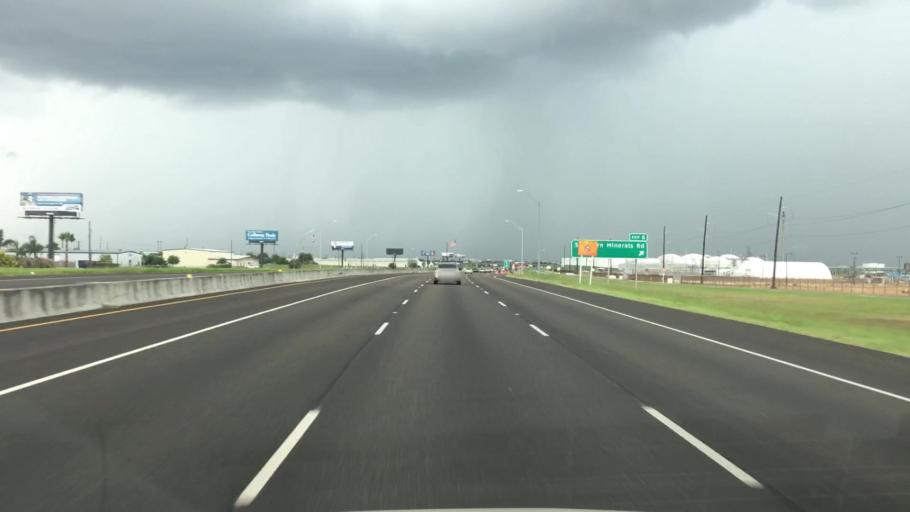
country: US
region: Texas
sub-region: Nueces County
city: Corpus Christi
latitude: 27.8067
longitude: -97.4916
